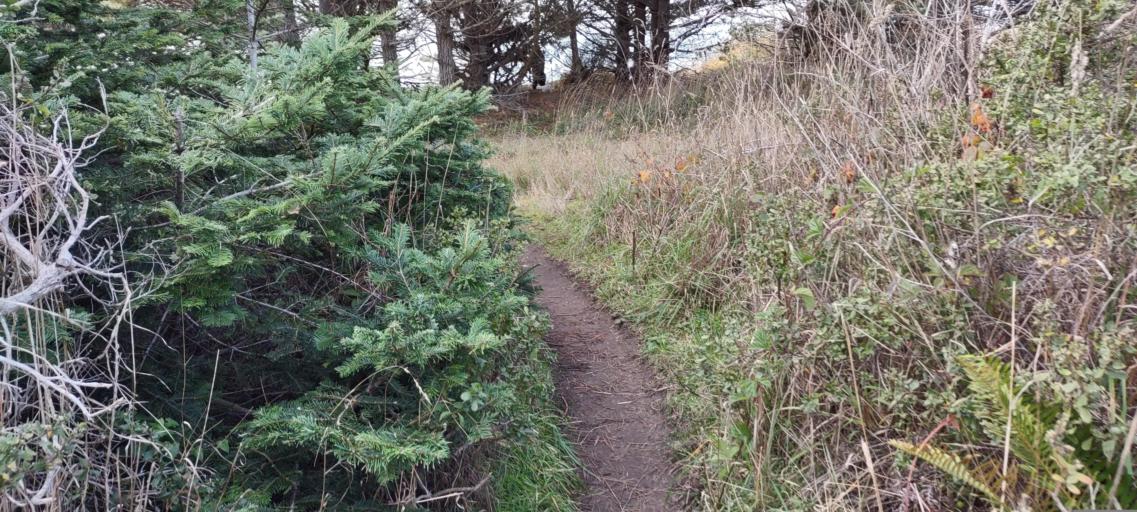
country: US
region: California
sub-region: Mendocino County
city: Fort Bragg
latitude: 39.3033
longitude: -123.7983
